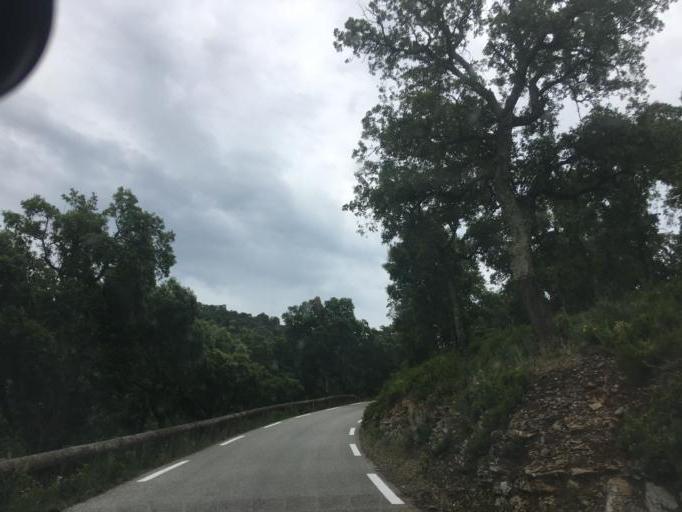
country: FR
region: Provence-Alpes-Cote d'Azur
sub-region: Departement du Var
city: Pierrefeu-du-Var
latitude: 43.2177
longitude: 6.2189
